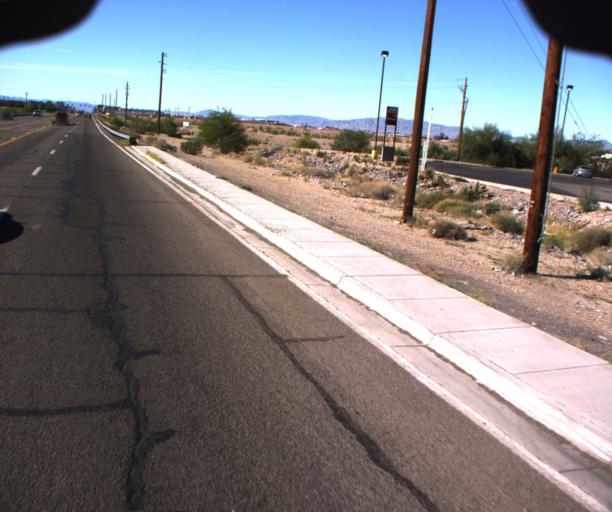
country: US
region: Arizona
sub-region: Mohave County
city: Mohave Valley
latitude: 35.0163
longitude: -114.5981
